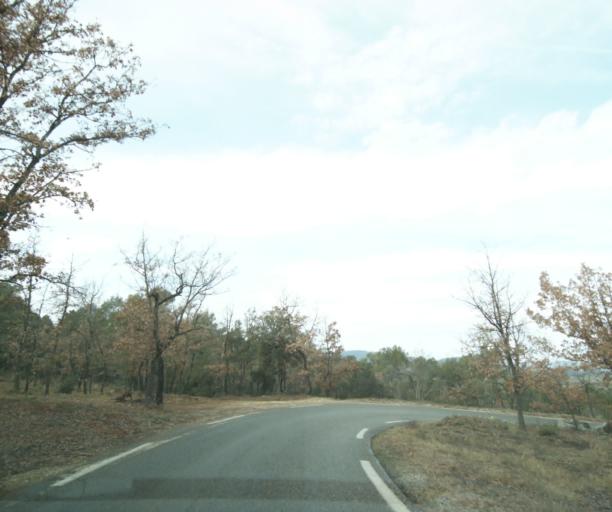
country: FR
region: Provence-Alpes-Cote d'Azur
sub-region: Departement du Var
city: Tourves
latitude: 43.3798
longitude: 5.8947
